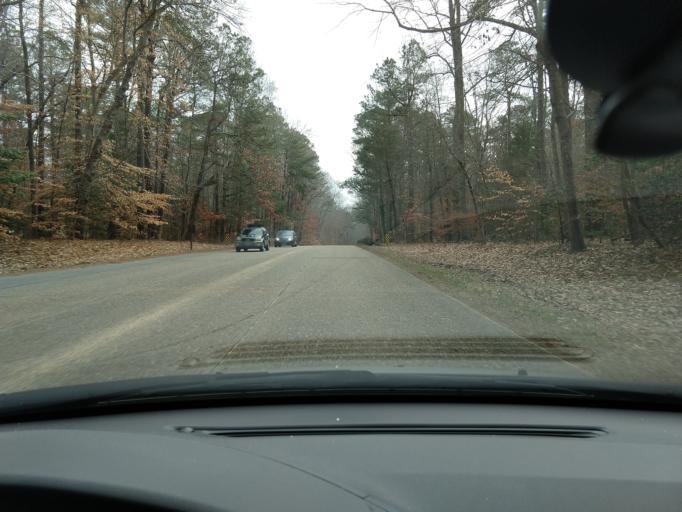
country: US
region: Virginia
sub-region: City of Williamsburg
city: Williamsburg
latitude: 37.2789
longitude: -76.6734
